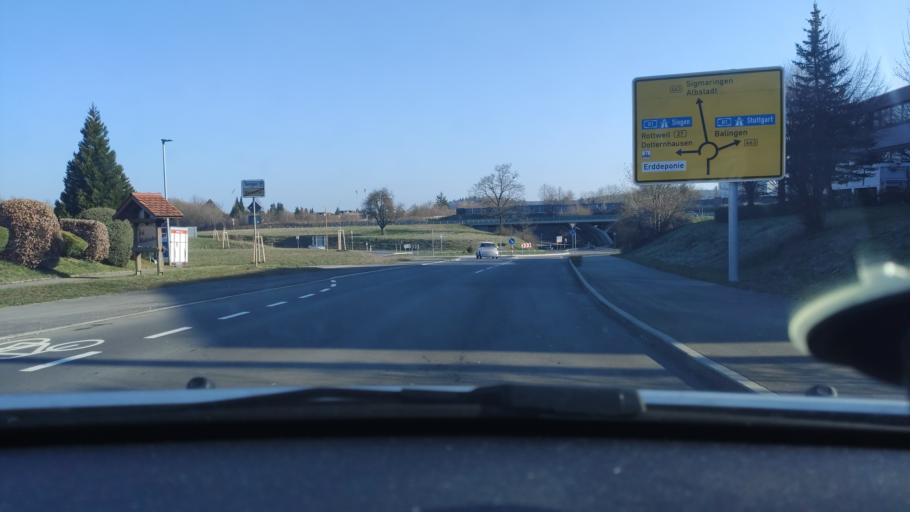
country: DE
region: Baden-Wuerttemberg
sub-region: Tuebingen Region
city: Balingen
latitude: 48.2435
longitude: 8.8543
